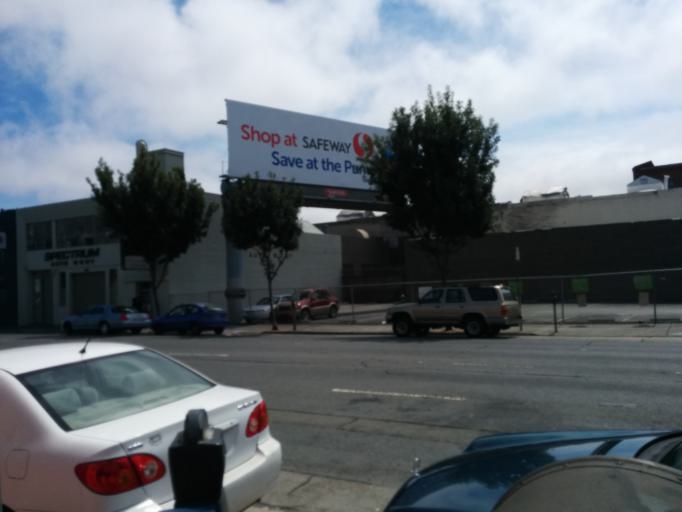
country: US
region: California
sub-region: San Francisco County
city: San Francisco
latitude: 37.7729
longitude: -122.4127
